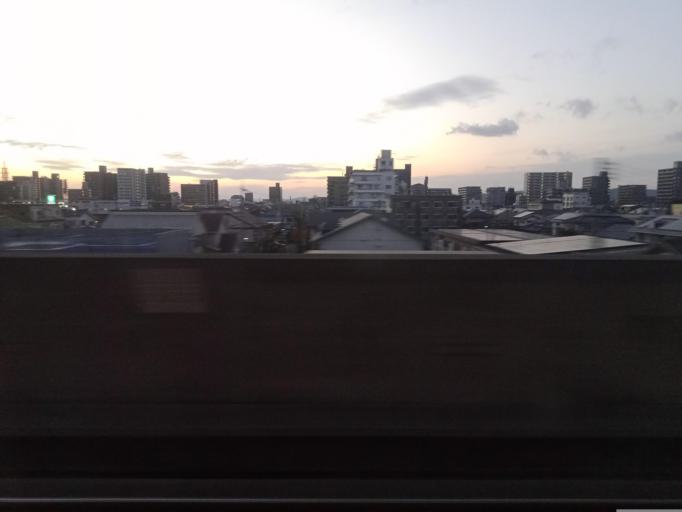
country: JP
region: Okayama
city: Okayama-shi
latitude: 34.6522
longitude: 133.9102
